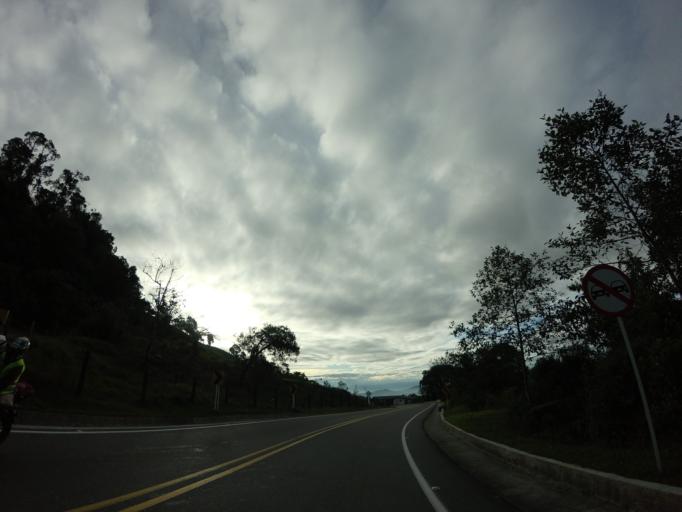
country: CO
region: Tolima
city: Herveo
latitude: 5.1062
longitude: -75.2735
